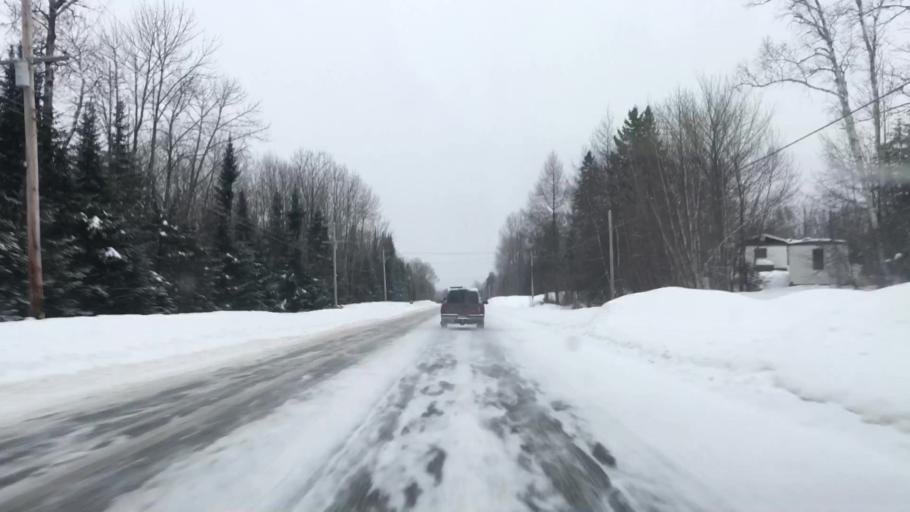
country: US
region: Maine
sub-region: Penobscot County
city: Medway
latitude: 45.5868
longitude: -68.4348
